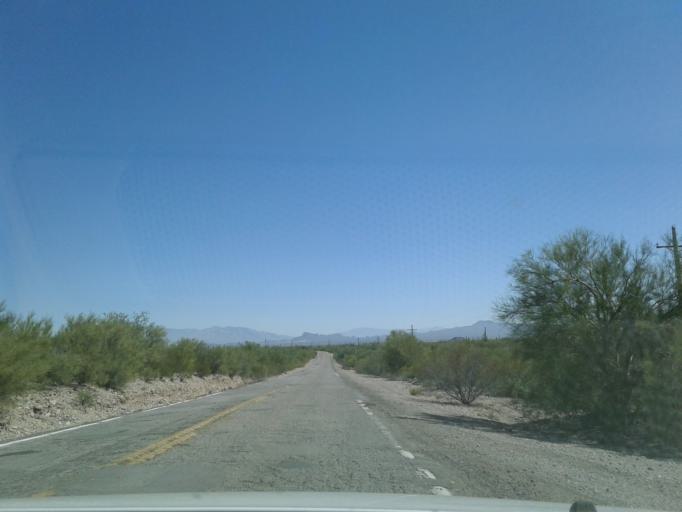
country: US
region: Arizona
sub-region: Pima County
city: Avra Valley
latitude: 32.3717
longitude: -111.4392
